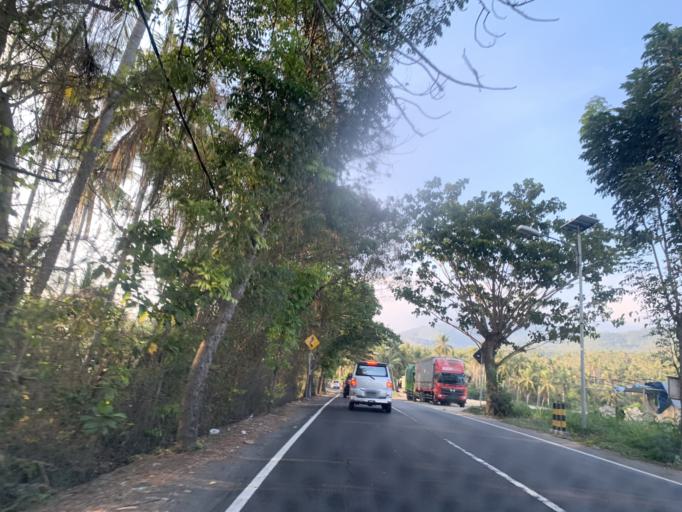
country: ID
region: Bali
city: Banjar Delodrurung
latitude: -8.4879
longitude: 114.9504
